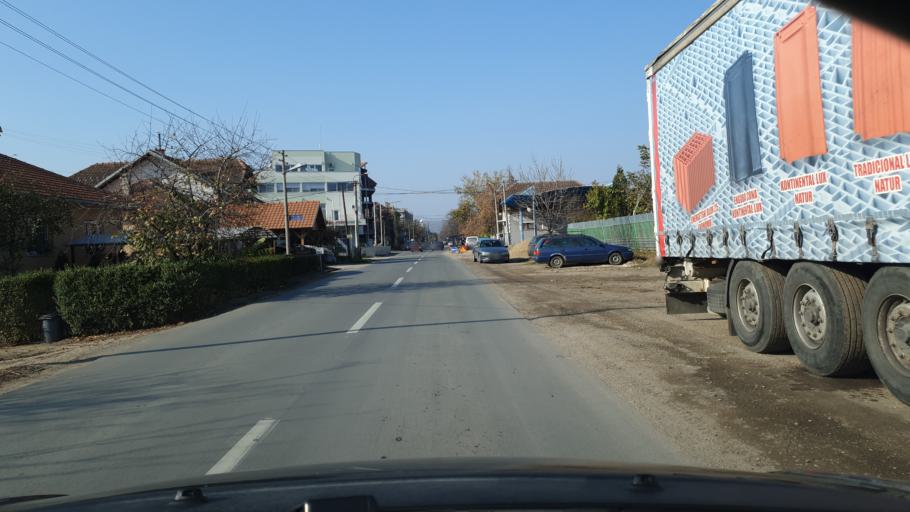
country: RS
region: Central Serbia
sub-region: Borski Okrug
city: Negotin
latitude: 44.2277
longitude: 22.5413
